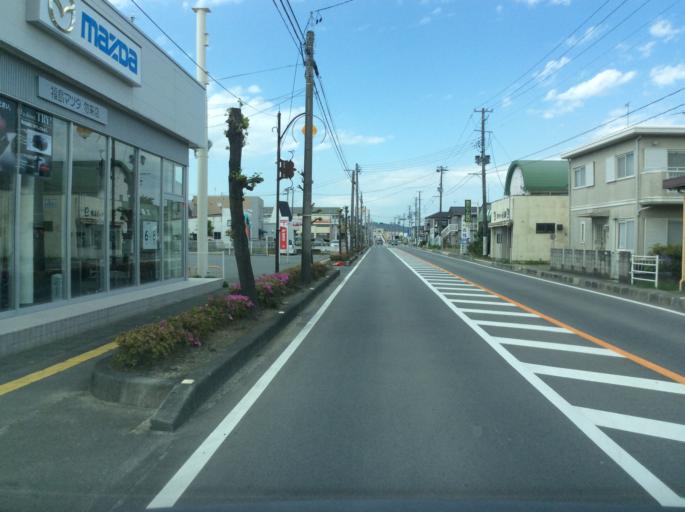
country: JP
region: Ibaraki
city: Kitaibaraki
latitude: 36.9038
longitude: 140.7880
